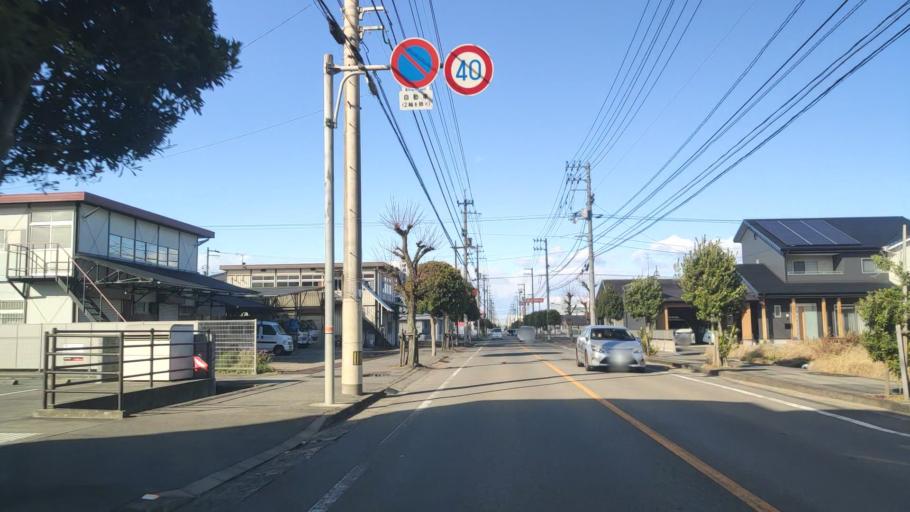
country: JP
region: Ehime
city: Saijo
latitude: 33.9227
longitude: 133.1915
